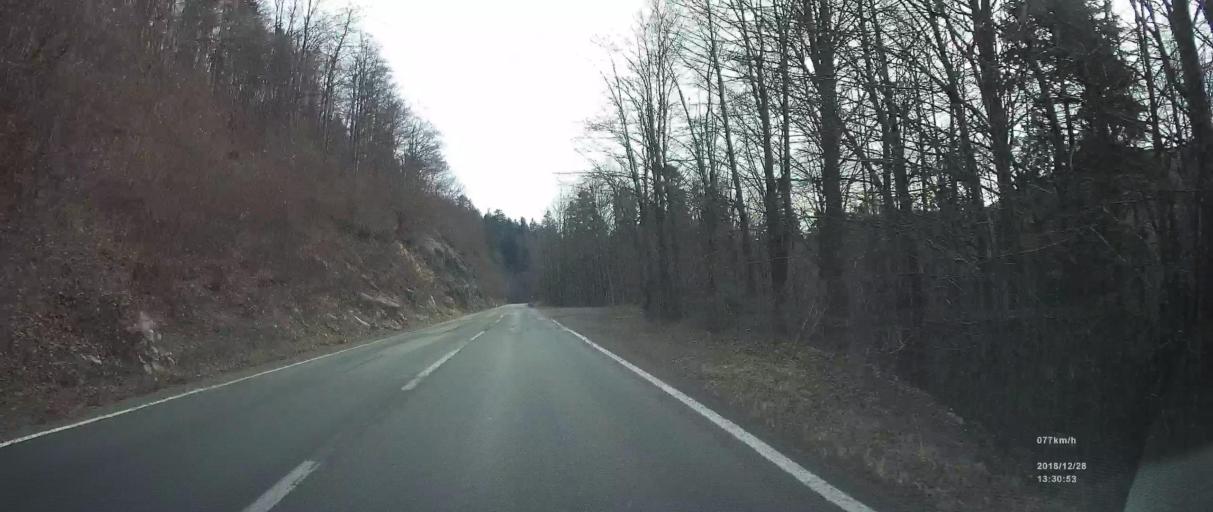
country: HR
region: Primorsko-Goranska
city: Hreljin
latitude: 45.3545
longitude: 14.6460
